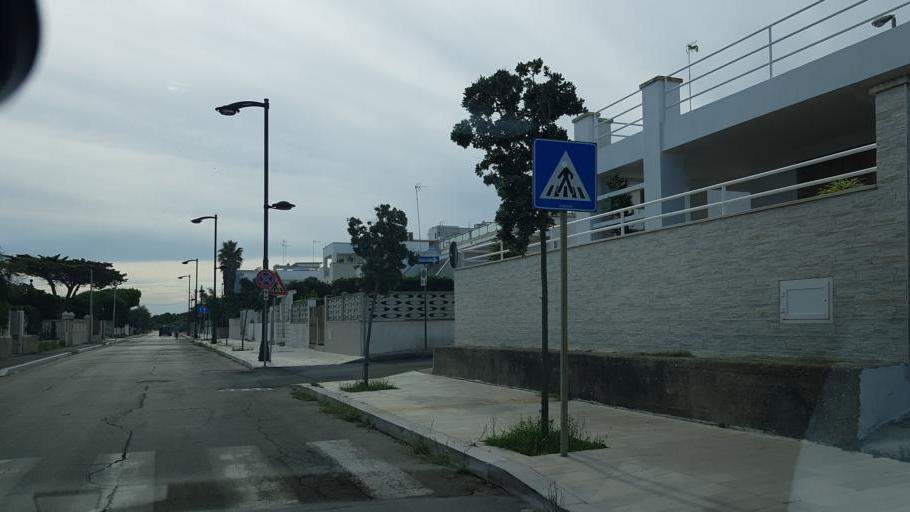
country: IT
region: Apulia
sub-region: Provincia di Lecce
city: Borgagne
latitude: 40.2999
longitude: 18.4069
